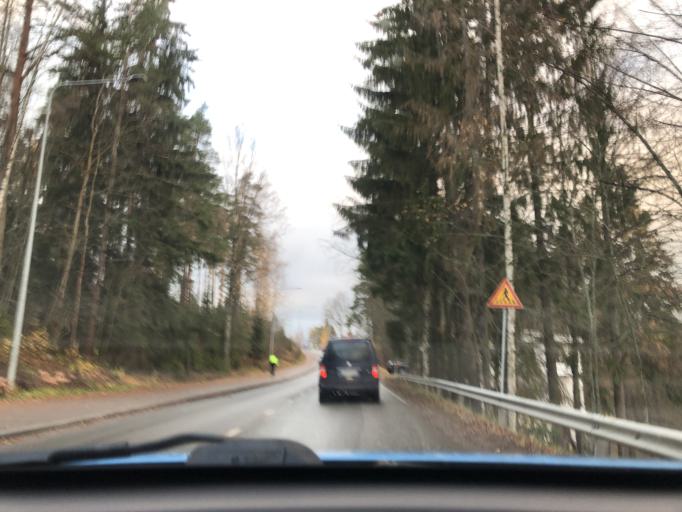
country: FI
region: Pirkanmaa
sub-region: Tampere
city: Kangasala
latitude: 61.4661
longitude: 24.0672
